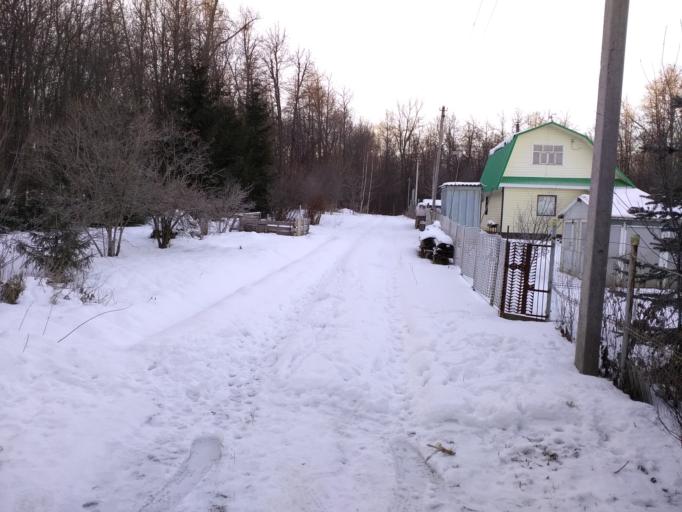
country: RU
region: Bashkortostan
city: Kudeyevskiy
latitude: 54.8055
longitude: 56.5942
